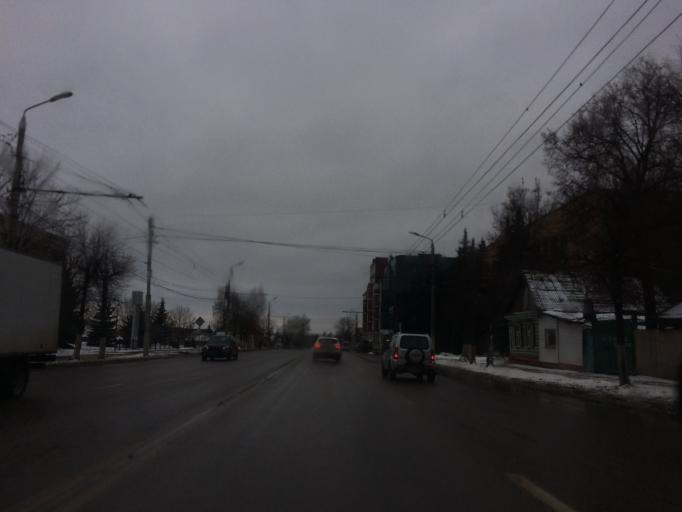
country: RU
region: Tula
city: Mendeleyevskiy
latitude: 54.1804
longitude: 37.5734
